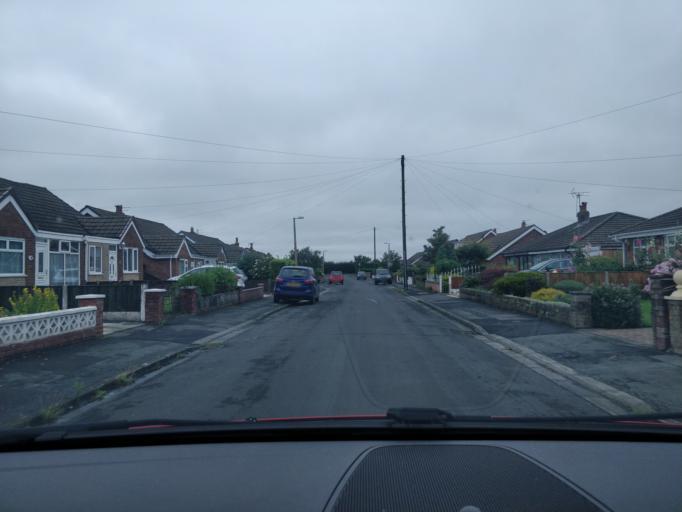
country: GB
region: England
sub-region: Lancashire
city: Banks
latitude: 53.6758
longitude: -2.9314
